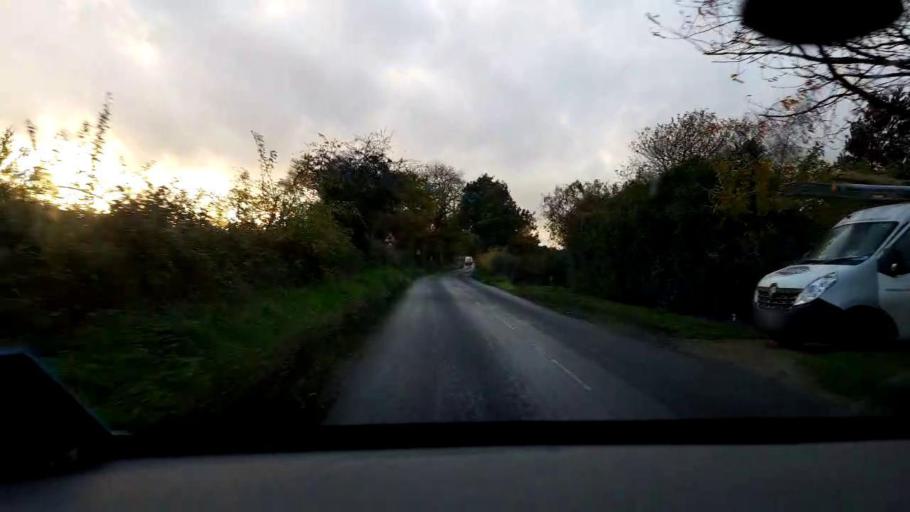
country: GB
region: England
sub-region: Norfolk
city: Spixworth
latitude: 52.6925
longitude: 1.3121
